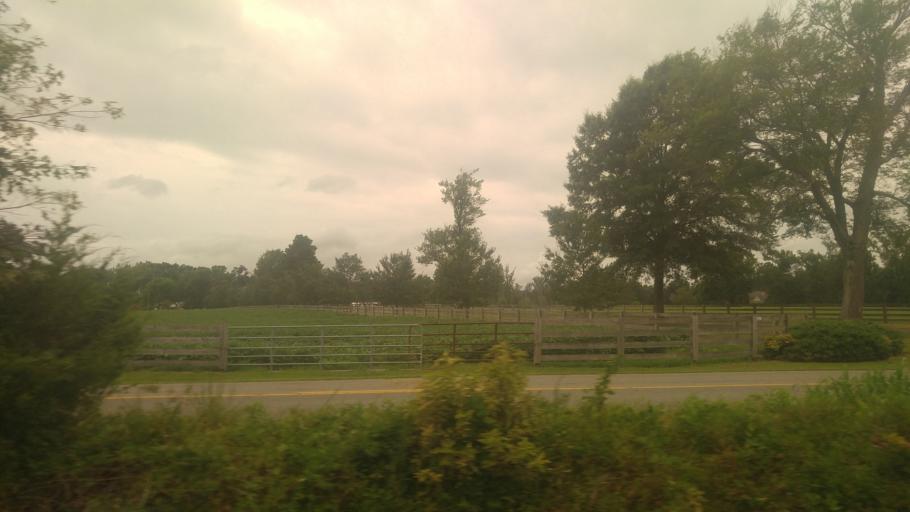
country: US
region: Virginia
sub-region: Hanover County
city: Ashland
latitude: 37.7421
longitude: -77.4864
